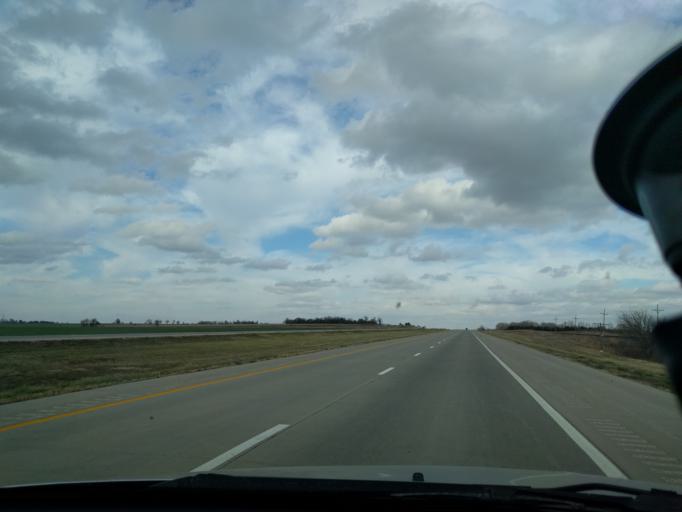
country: US
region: Kansas
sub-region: Reno County
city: Buhler
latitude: 38.1616
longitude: -97.8344
